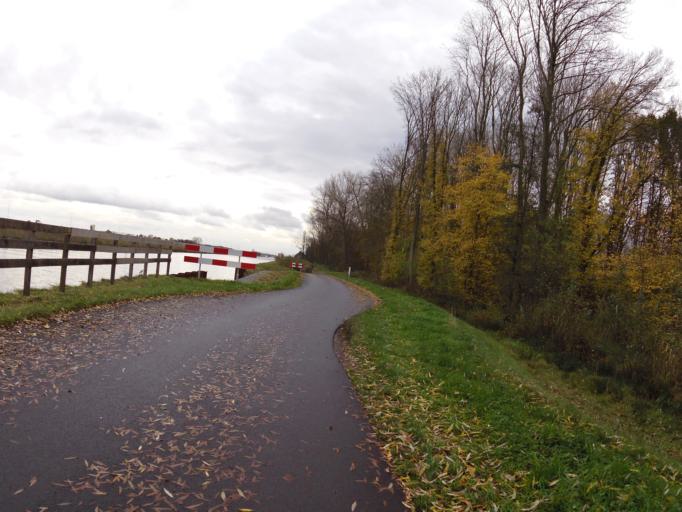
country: NL
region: North Brabant
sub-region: Gemeente Sint-Michielsgestel
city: Sint-Michielsgestel
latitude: 51.6789
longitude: 5.3757
